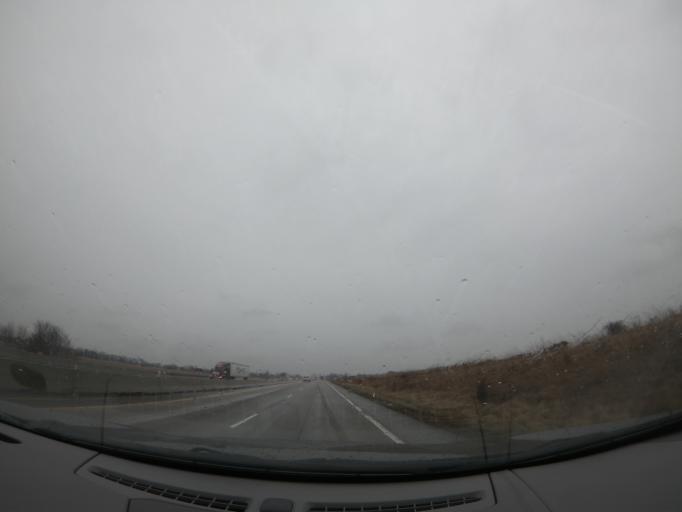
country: US
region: Kentucky
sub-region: Larue County
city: Hodgenville
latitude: 37.5530
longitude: -85.8783
